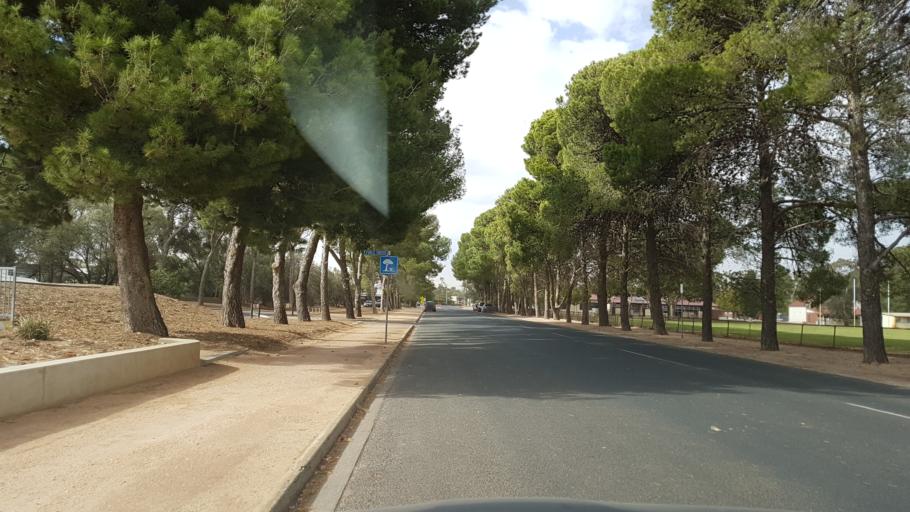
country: AU
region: South Australia
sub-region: Wakefield
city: Balaklava
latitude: -34.1493
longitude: 138.4164
